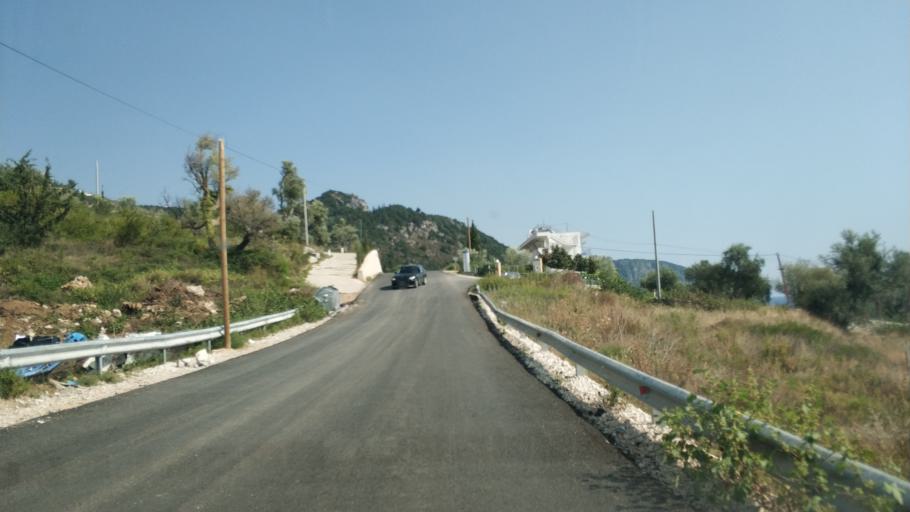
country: AL
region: Vlore
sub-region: Rrethi i Vlores
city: Vranisht
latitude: 40.1445
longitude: 19.6370
